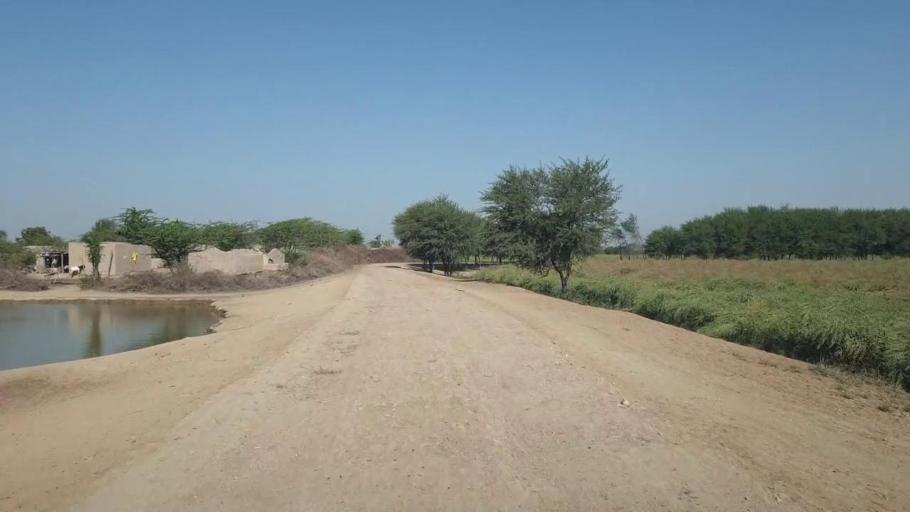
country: PK
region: Sindh
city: Umarkot
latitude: 25.3023
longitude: 69.6534
